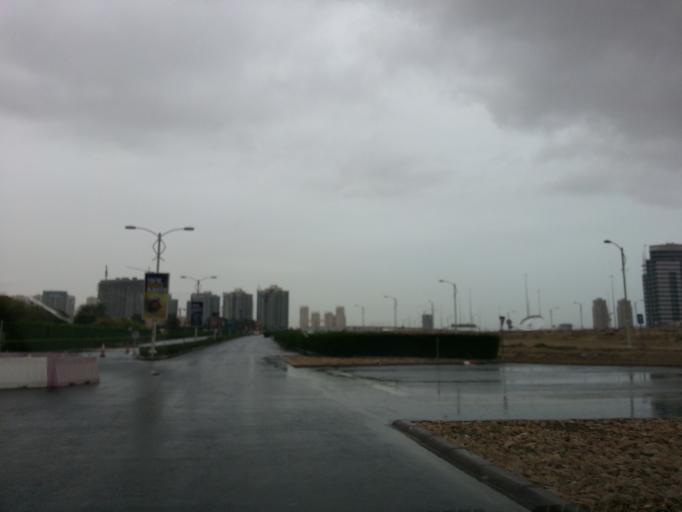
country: AE
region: Dubai
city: Dubai
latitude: 25.0446
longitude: 55.2126
